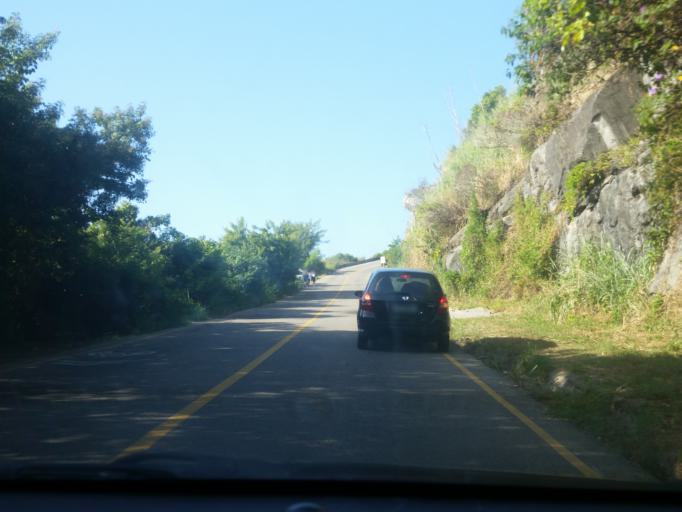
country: BR
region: Rio de Janeiro
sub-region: Nilopolis
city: Nilopolis
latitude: -23.0440
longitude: -43.5075
